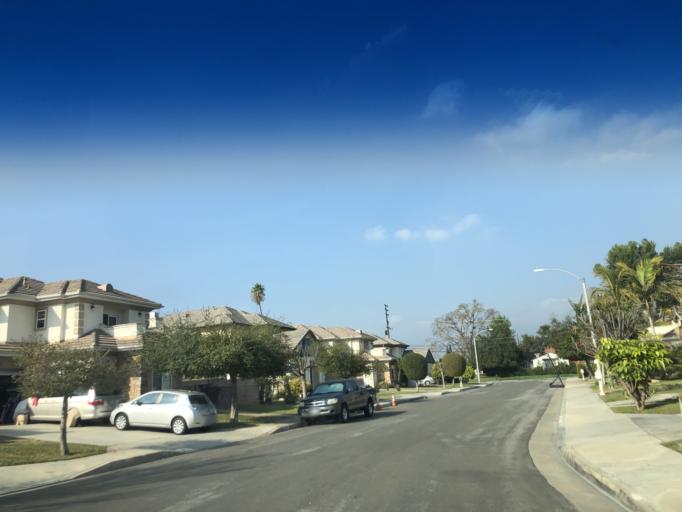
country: US
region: California
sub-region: Los Angeles County
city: San Marino
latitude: 34.1125
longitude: -118.0878
